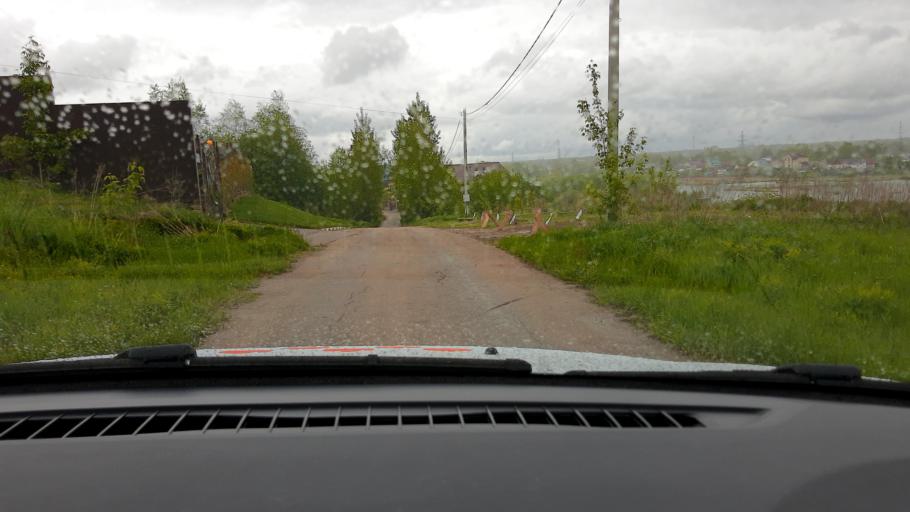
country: RU
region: Nizjnij Novgorod
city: Afonino
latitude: 56.2655
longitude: 44.0985
